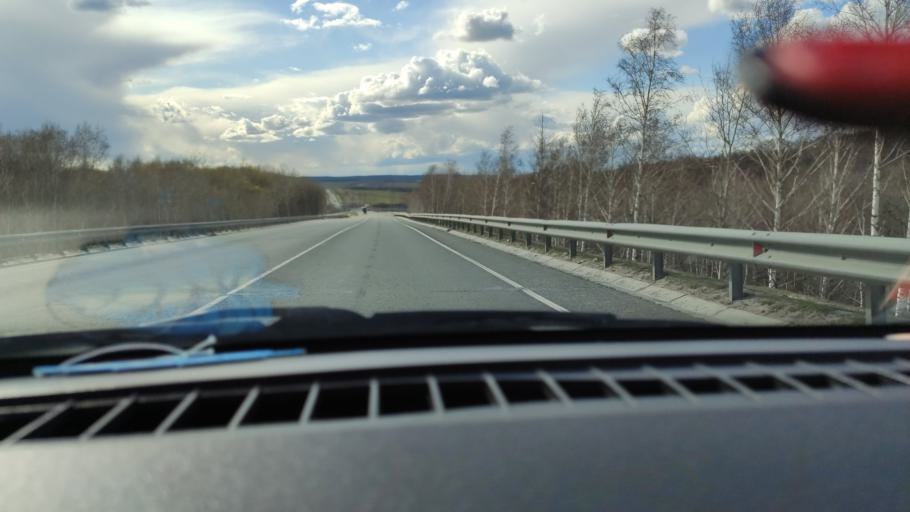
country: RU
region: Saratov
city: Vol'sk
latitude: 52.1142
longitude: 47.3082
